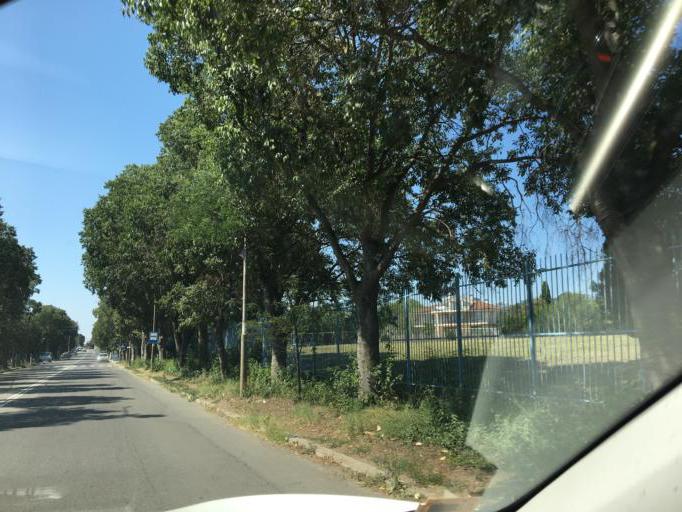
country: BG
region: Burgas
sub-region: Obshtina Kameno
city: Kameno
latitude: 42.6080
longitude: 27.3892
